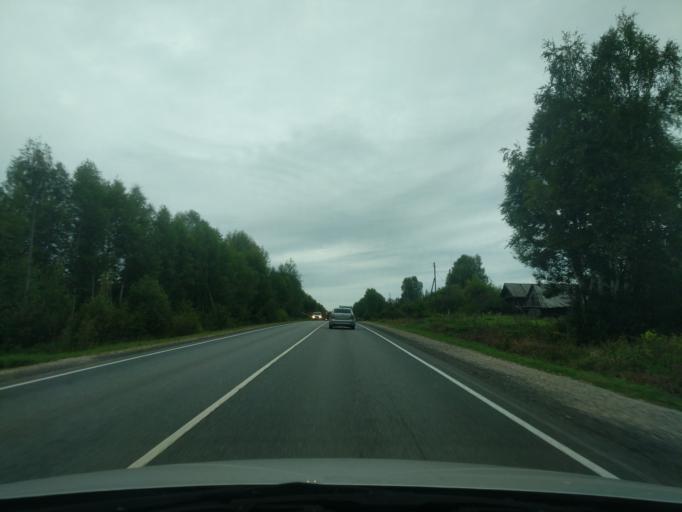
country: RU
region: Kirov
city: Orlov
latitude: 58.5395
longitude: 48.7886
